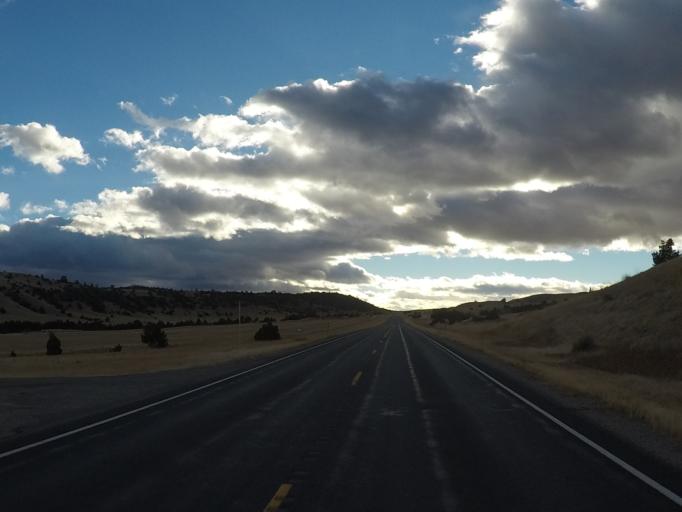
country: US
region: Montana
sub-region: Jefferson County
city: Whitehall
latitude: 45.9102
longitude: -111.9411
